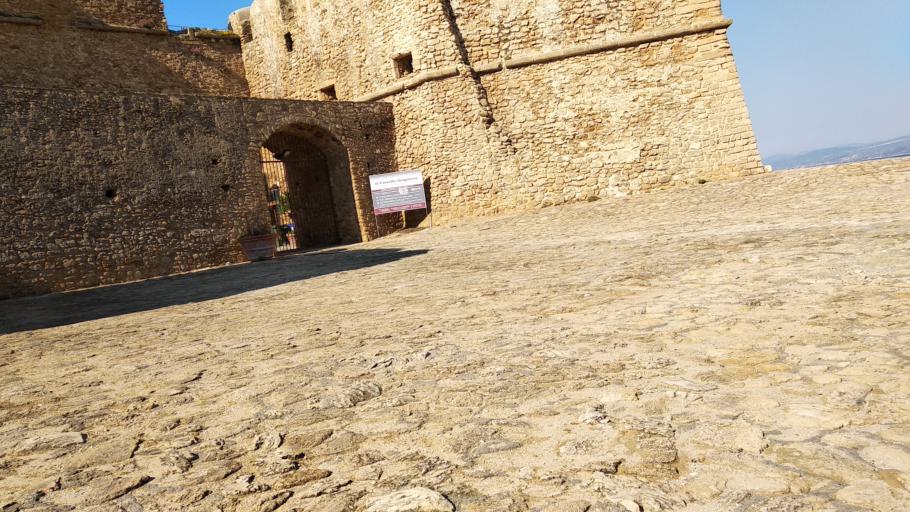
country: IT
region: Calabria
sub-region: Provincia di Crotone
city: Le Castella
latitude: 38.9073
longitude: 17.0216
